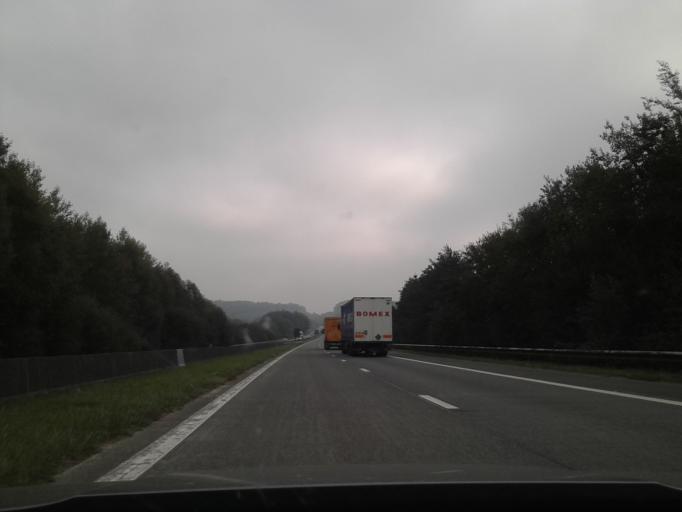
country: BE
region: Wallonia
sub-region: Province du Hainaut
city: Frasnes-lez-Buissenal
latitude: 50.6584
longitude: 3.6488
